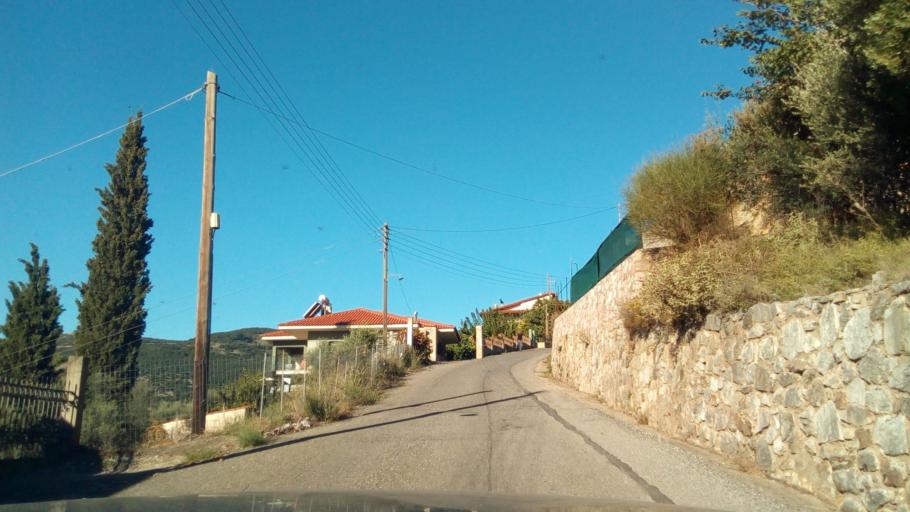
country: GR
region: West Greece
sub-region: Nomos Aitolias kai Akarnanias
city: Nafpaktos
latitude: 38.4214
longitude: 21.8443
